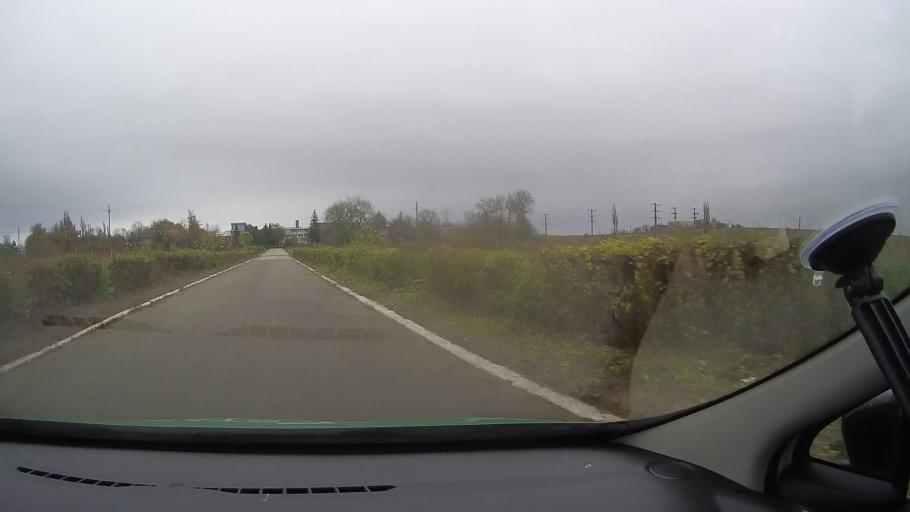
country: RO
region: Constanta
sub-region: Oras Murfatlar
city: Murfatlar
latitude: 44.1750
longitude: 28.4228
